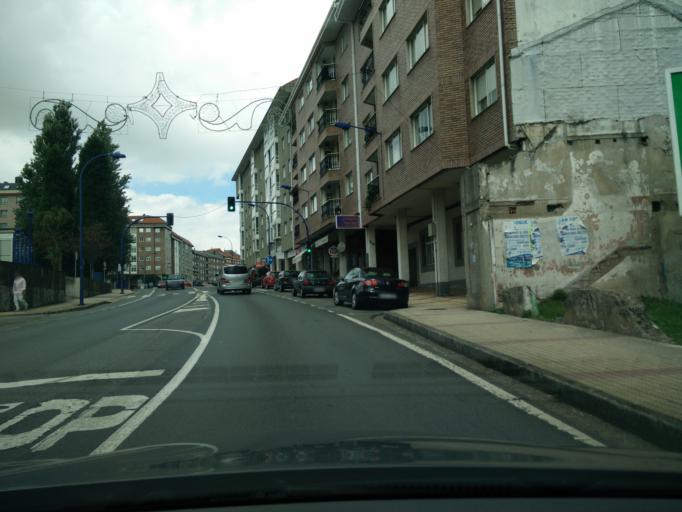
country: ES
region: Galicia
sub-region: Provincia da Coruna
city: Culleredo
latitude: 43.3170
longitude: -8.3836
